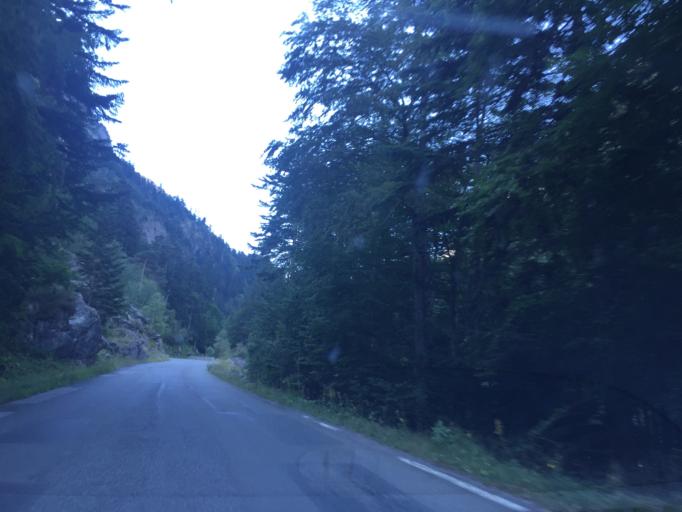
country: FR
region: Midi-Pyrenees
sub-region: Departement des Hautes-Pyrenees
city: Cauterets
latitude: 42.8667
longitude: -0.1152
